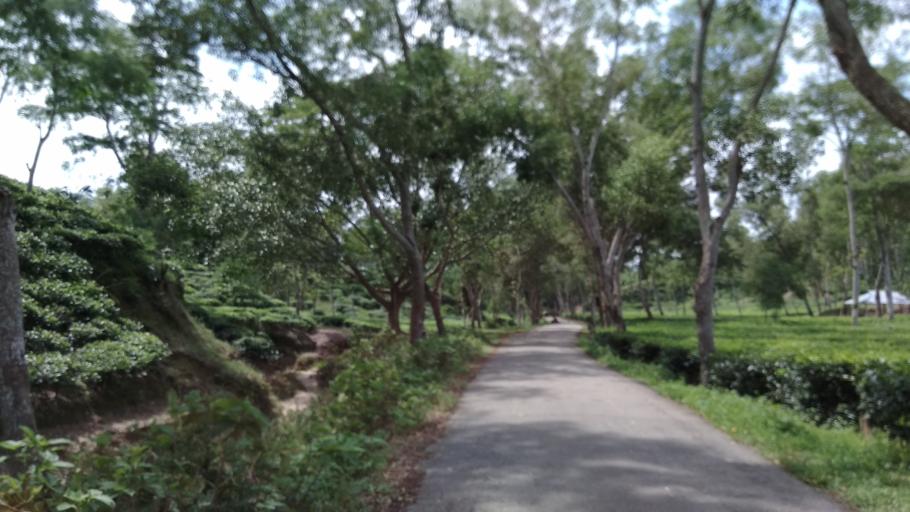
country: IN
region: Tripura
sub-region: Dhalai
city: Kamalpur
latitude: 24.3020
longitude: 91.8195
